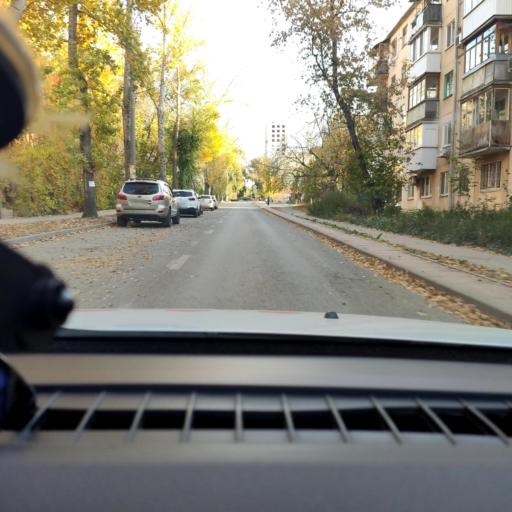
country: RU
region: Samara
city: Samara
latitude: 53.2135
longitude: 50.1575
